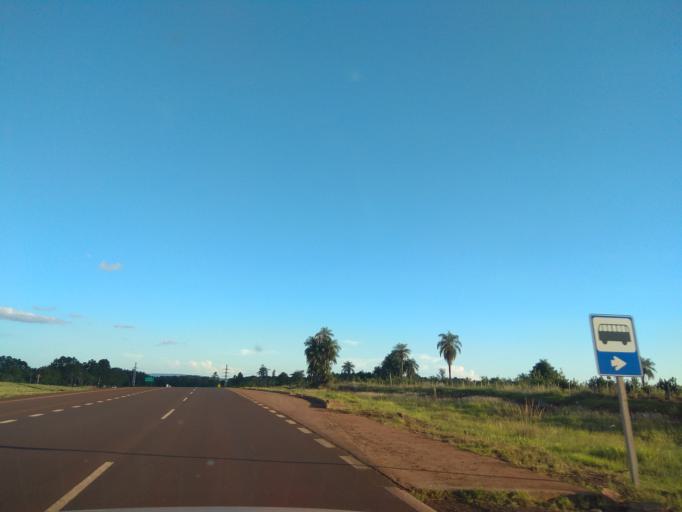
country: AR
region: Misiones
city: Garupa
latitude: -27.5346
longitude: -55.8560
